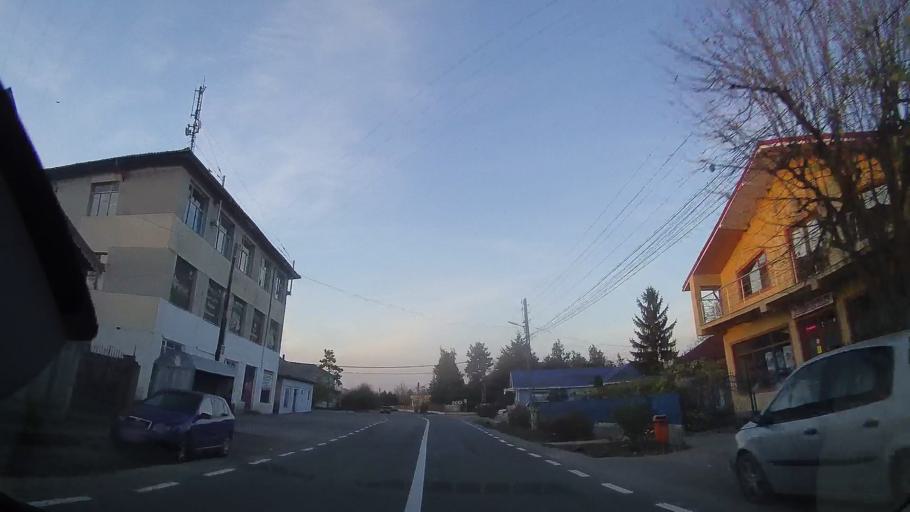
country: RO
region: Constanta
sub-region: Comuna Mereni
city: Mereni
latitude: 44.0317
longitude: 28.3844
